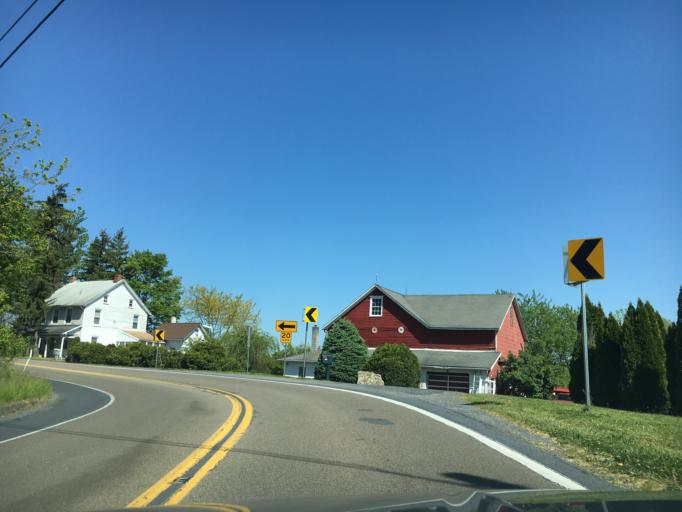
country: US
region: Pennsylvania
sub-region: Lehigh County
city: Catasauqua
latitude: 40.6748
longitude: -75.4287
